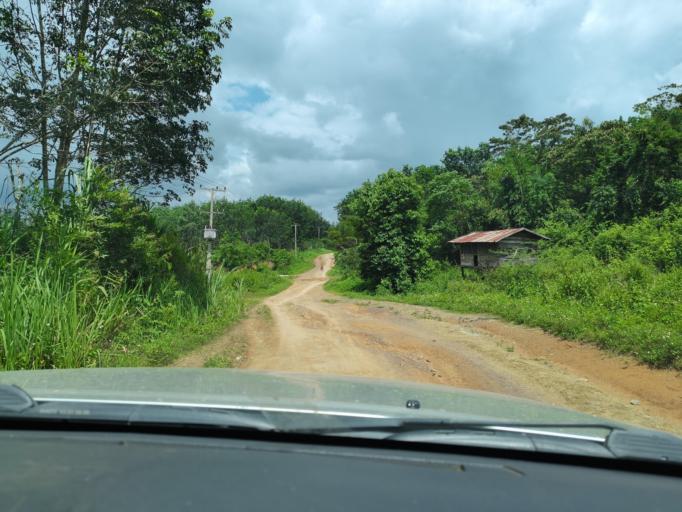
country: LA
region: Loungnamtha
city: Muang Long
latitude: 20.6849
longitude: 101.0459
